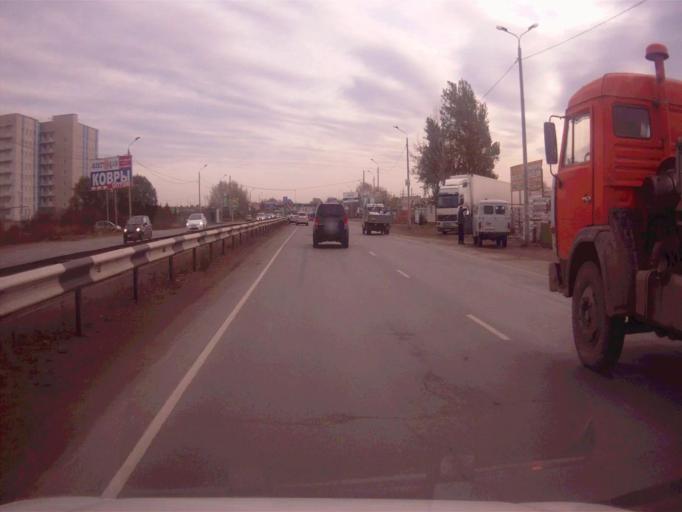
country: RU
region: Chelyabinsk
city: Novosineglazovskiy
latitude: 55.0658
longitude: 61.3959
